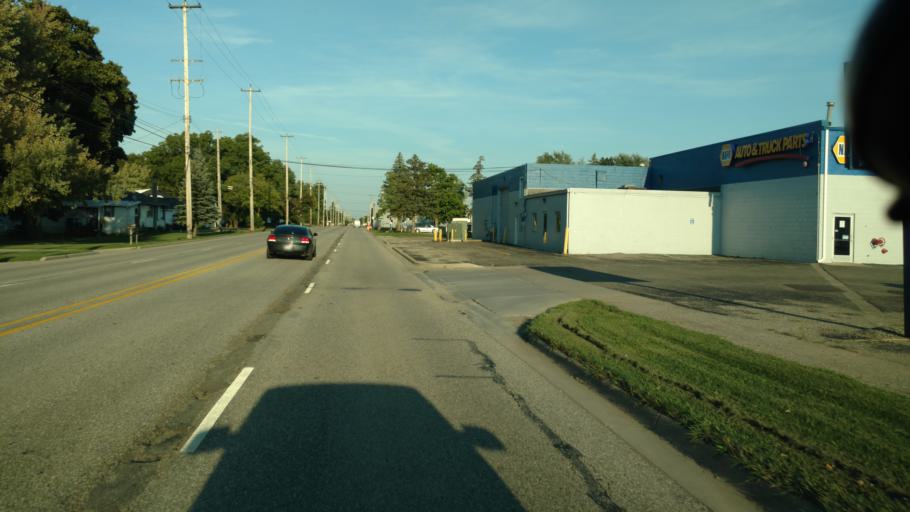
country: US
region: Michigan
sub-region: Ingham County
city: Edgemont Park
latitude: 42.7265
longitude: -84.5993
